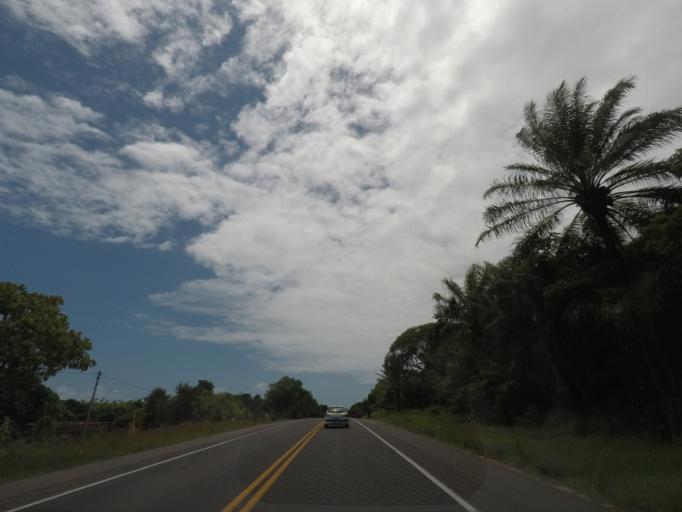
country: BR
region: Bahia
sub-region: Itaparica
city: Itaparica
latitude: -12.9562
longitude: -38.6324
